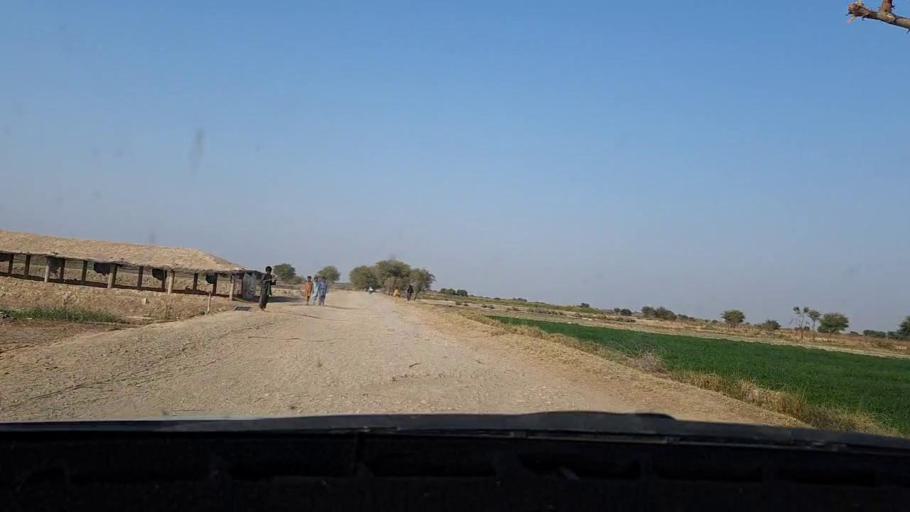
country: PK
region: Sindh
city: Tando Mittha Khan
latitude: 25.8430
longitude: 69.3326
